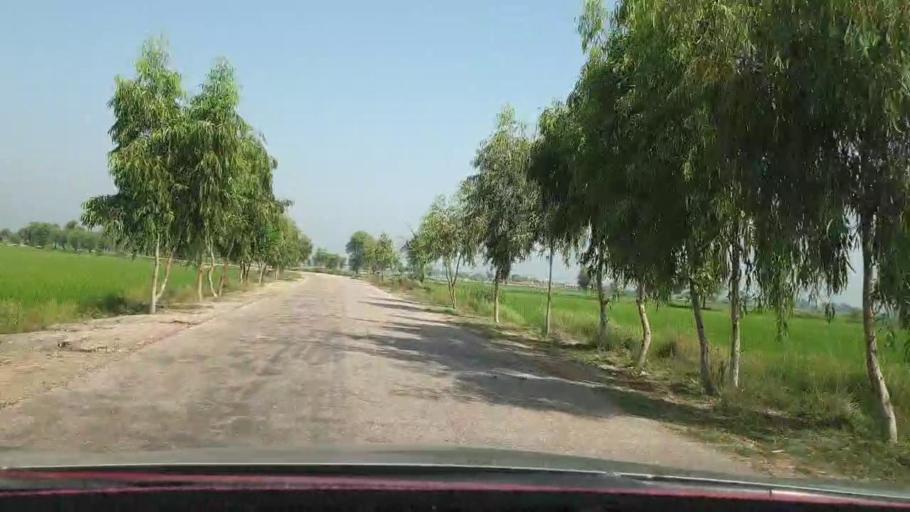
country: PK
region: Sindh
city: Warah
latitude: 27.4704
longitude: 67.8331
